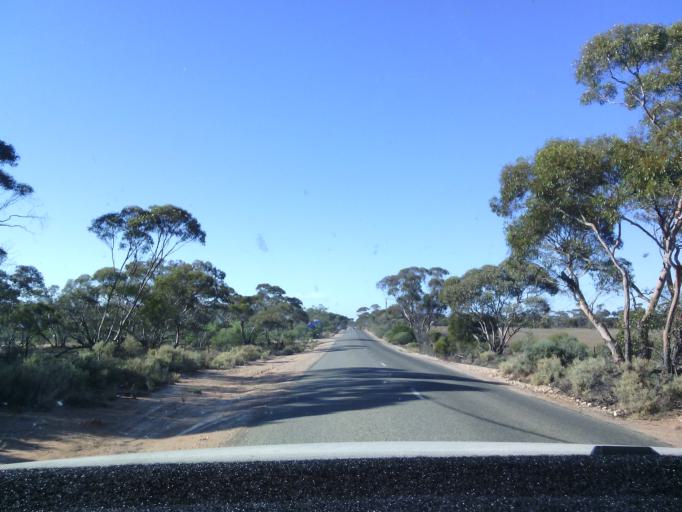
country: AU
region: South Australia
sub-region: Berri and Barmera
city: Monash
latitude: -34.2422
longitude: 140.5925
